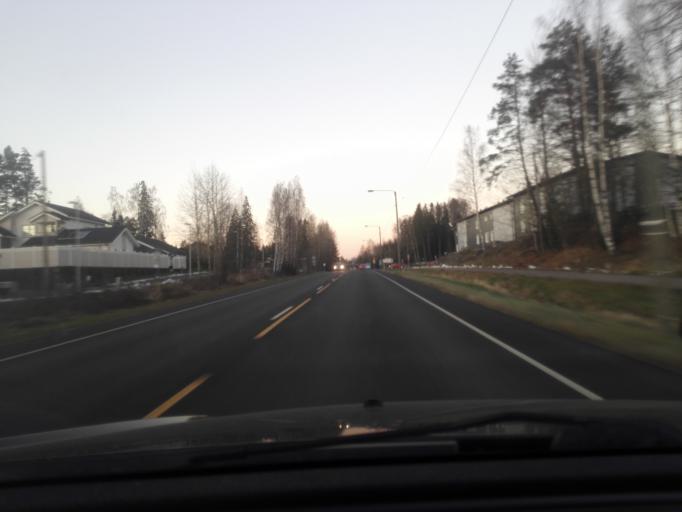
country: FI
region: Uusimaa
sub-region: Helsinki
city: Kerava
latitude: 60.3421
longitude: 25.1261
